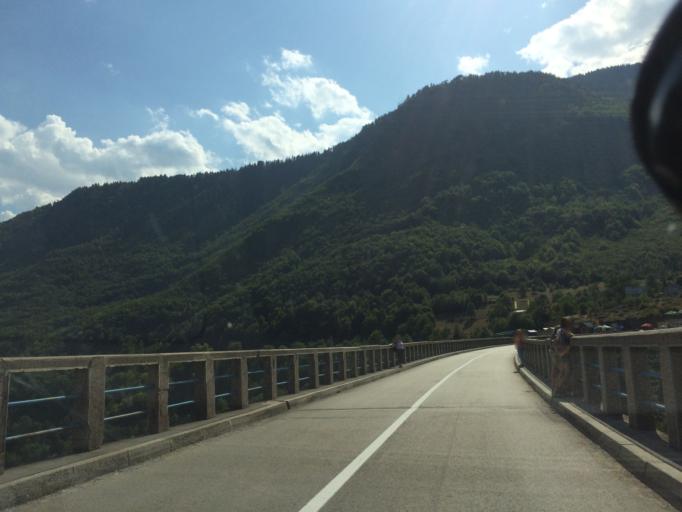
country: ME
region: Opstina Zabljak
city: Zabljak
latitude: 43.1500
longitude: 19.2948
